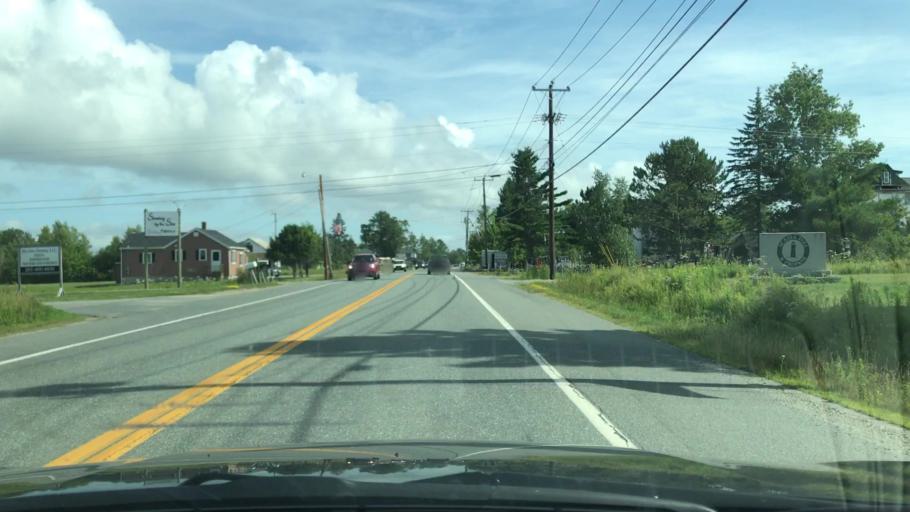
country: US
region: Maine
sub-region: Hancock County
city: Trenton
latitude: 44.4672
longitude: -68.3625
